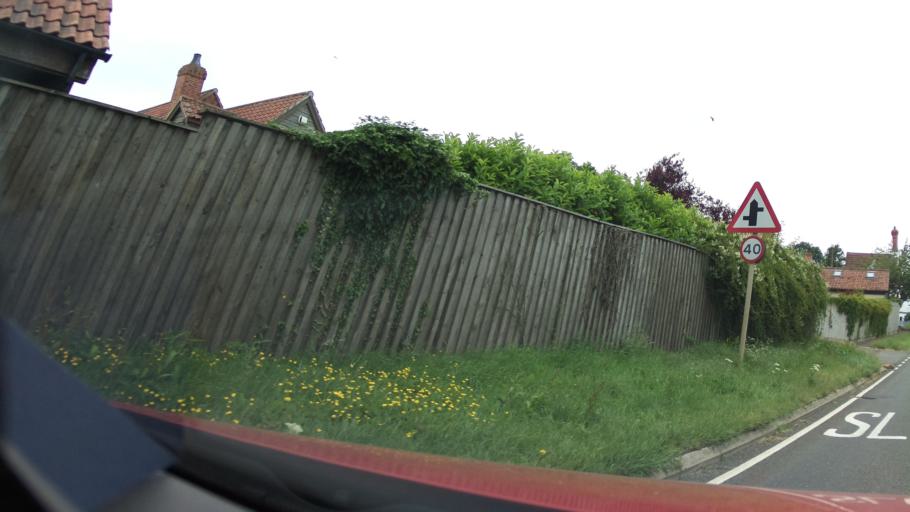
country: GB
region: England
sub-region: Leicestershire
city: Melton Mowbray
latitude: 52.7422
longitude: -0.8624
